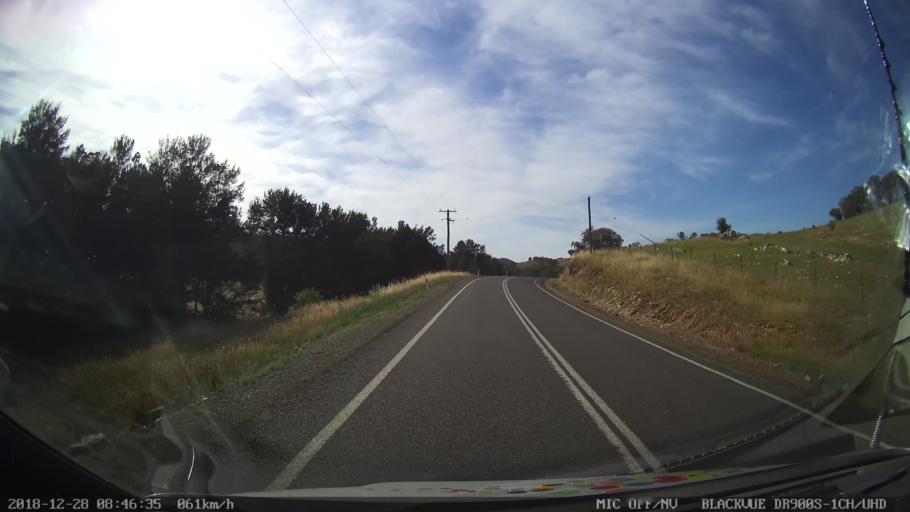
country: AU
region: New South Wales
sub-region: Upper Lachlan Shire
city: Crookwell
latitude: -34.0204
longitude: 149.3317
